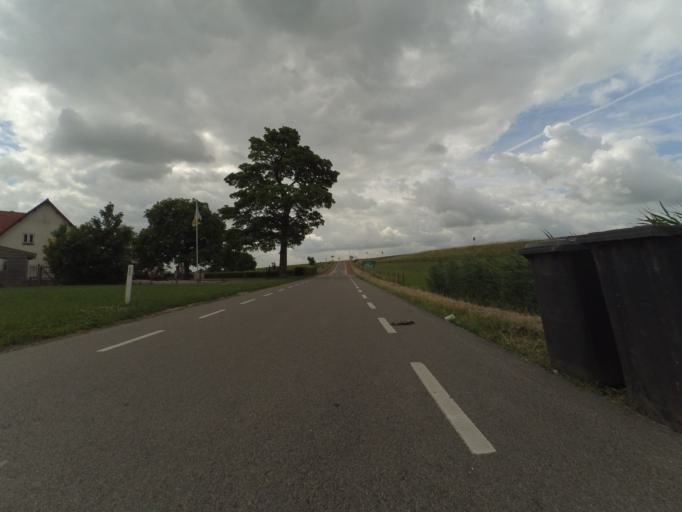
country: NL
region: Gelderland
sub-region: Gemeente Culemborg
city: Culemborg
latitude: 51.9813
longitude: 5.2551
